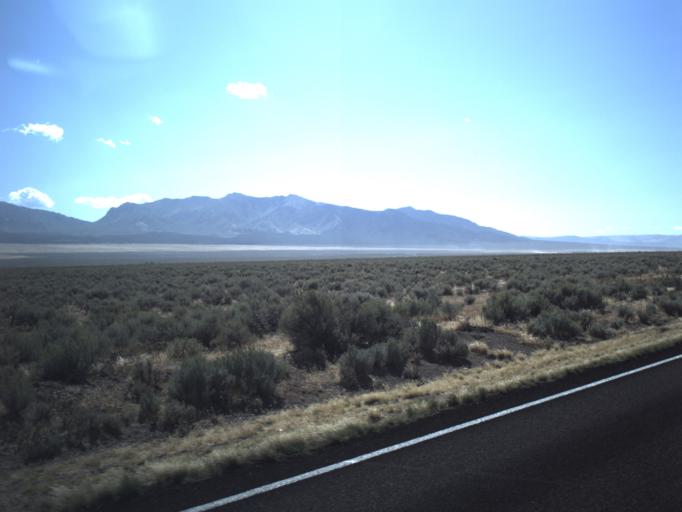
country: US
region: Utah
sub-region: Beaver County
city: Milford
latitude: 38.4248
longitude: -113.0099
